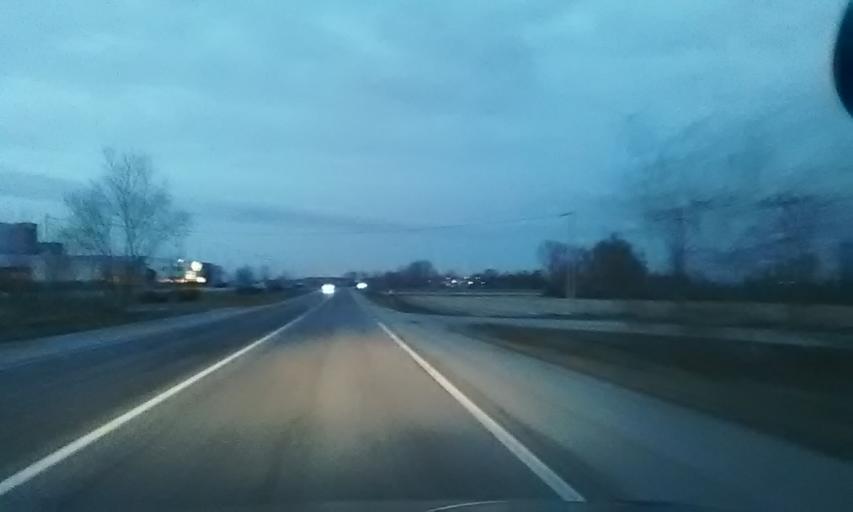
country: IT
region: Piedmont
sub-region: Provincia di Vercelli
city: Stroppiana
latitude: 45.2520
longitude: 8.4609
